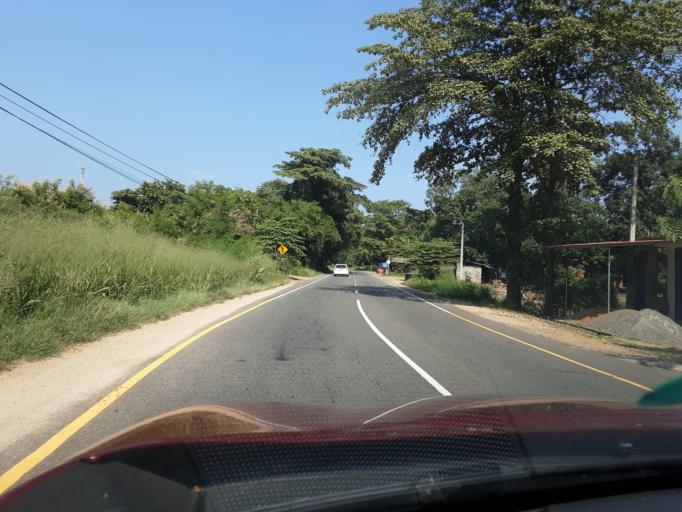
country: LK
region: Uva
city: Badulla
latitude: 7.2856
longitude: 81.0406
